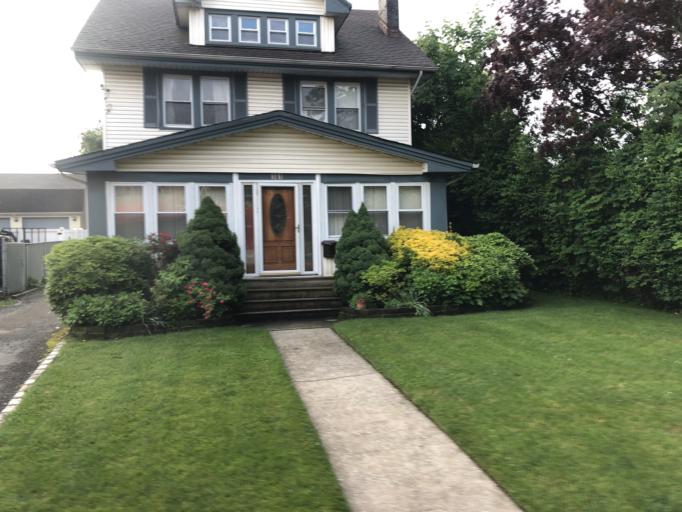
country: US
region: New York
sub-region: Nassau County
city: Rockville Centre
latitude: 40.6635
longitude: -73.6448
